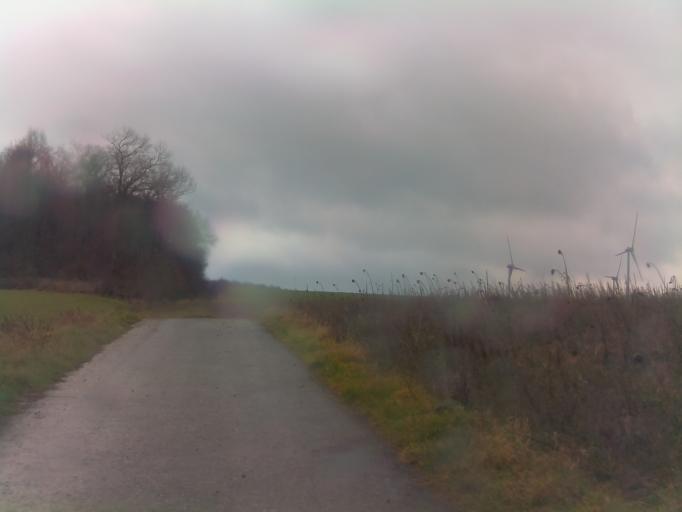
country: DE
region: Rheinland-Pfalz
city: Oberhausen an der Appel
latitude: 49.7122
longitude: 7.8733
